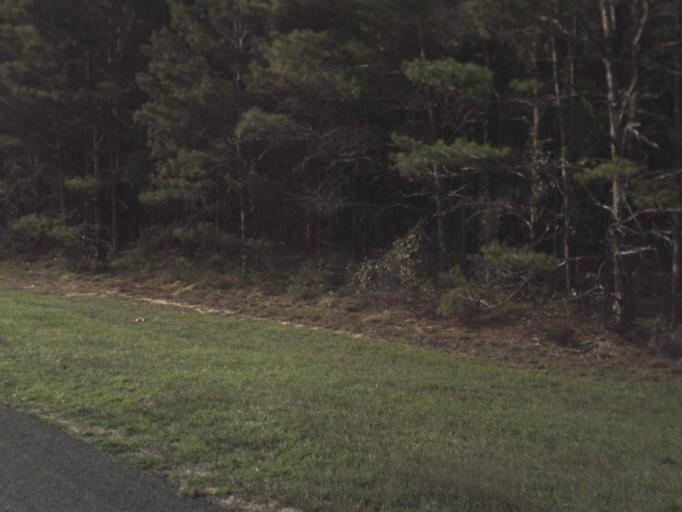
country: US
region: Florida
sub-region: Bay County
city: Youngstown
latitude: 30.4276
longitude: -85.6105
